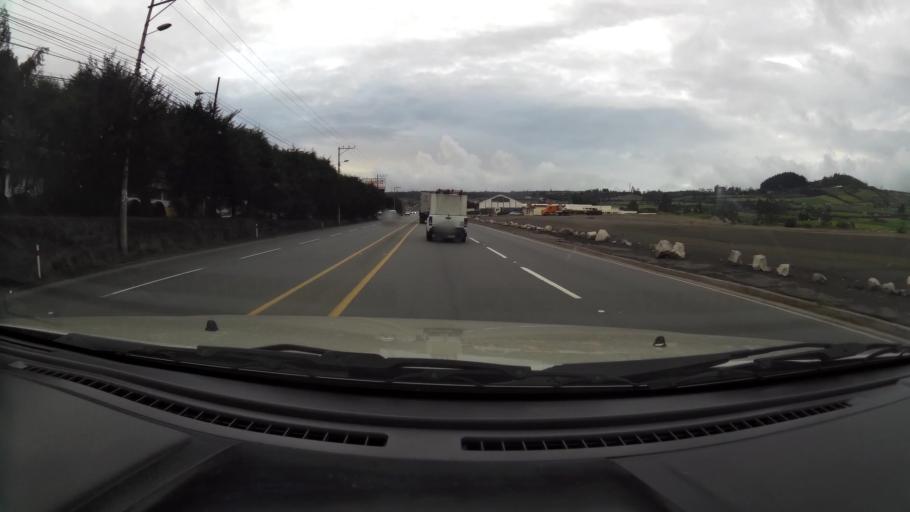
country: EC
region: Pichincha
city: Machachi
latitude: -0.4504
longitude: -78.6386
